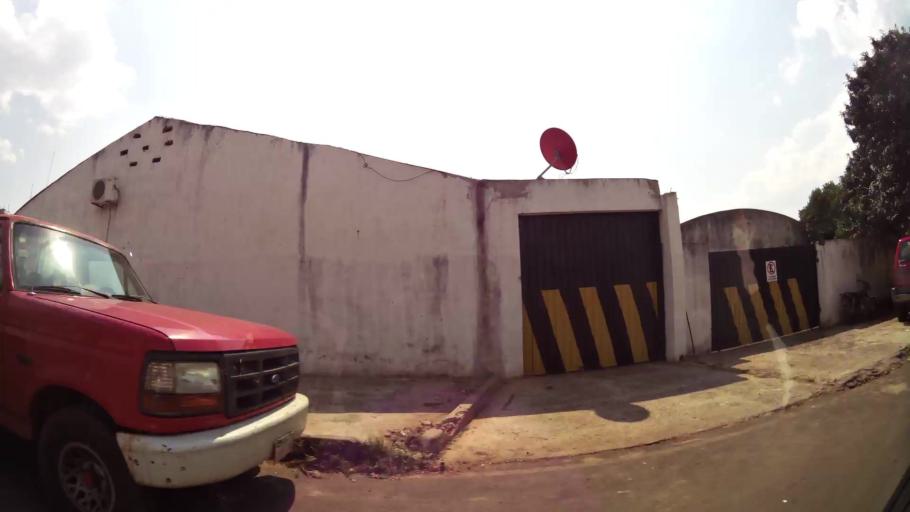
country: PY
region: Alto Parana
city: Ciudad del Este
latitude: -25.5098
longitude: -54.6387
